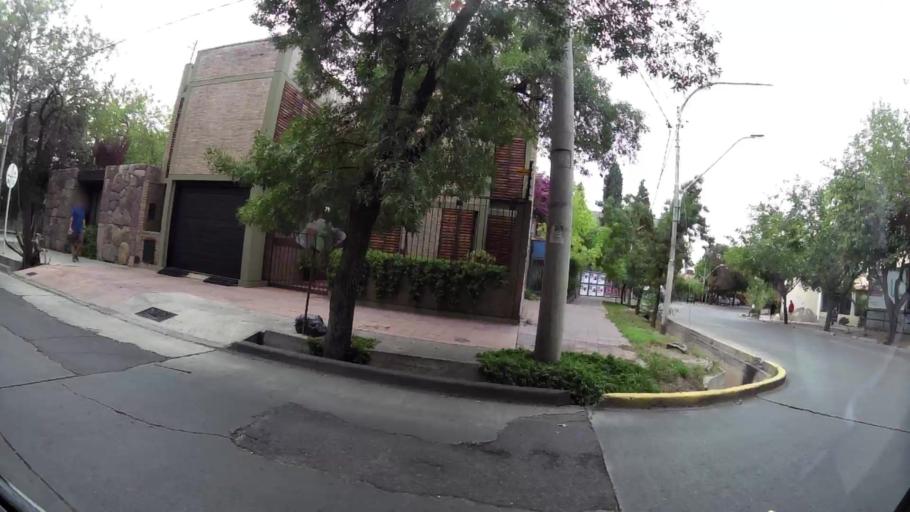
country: AR
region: Mendoza
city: Mendoza
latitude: -32.8961
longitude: -68.8575
